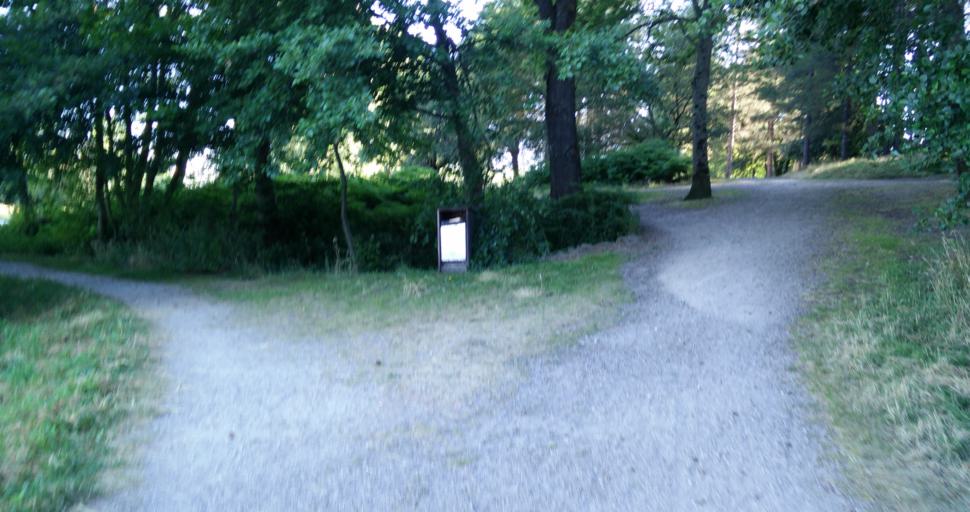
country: FR
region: Auvergne
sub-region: Departement de l'Allier
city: Yzeure
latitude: 46.5454
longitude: 3.3737
